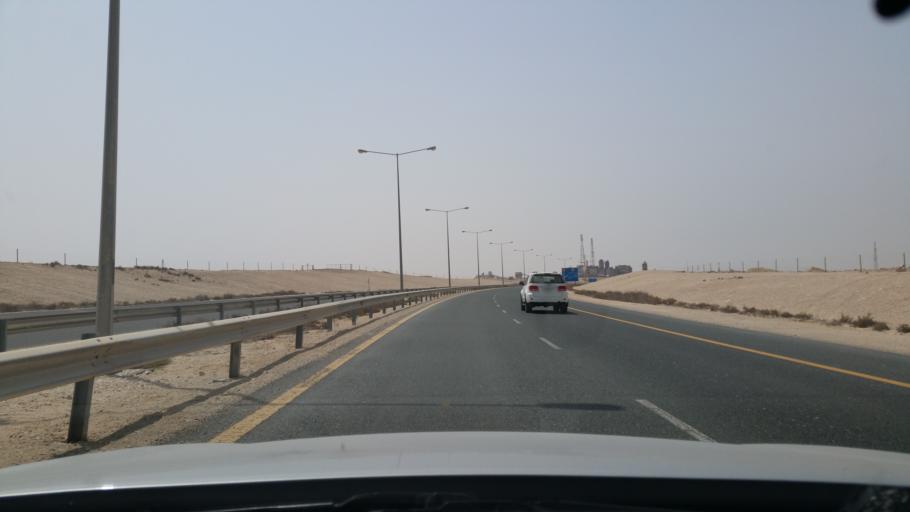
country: QA
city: Umm Bab
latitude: 25.2210
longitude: 50.8074
